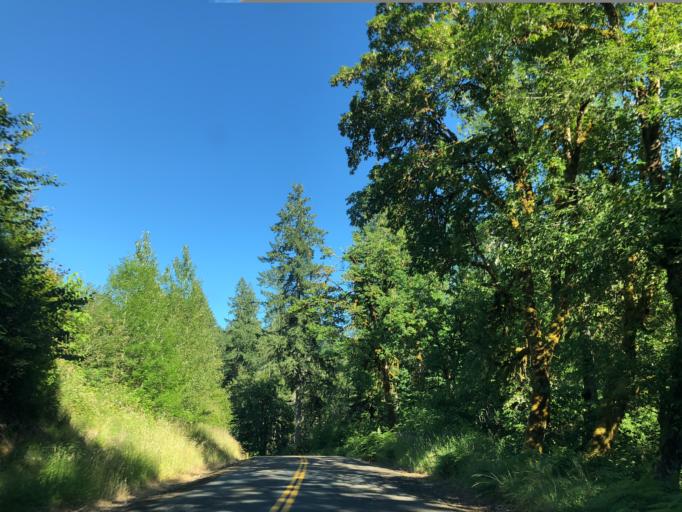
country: US
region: Oregon
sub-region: Linn County
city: Sweet Home
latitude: 44.4652
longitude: -122.6848
